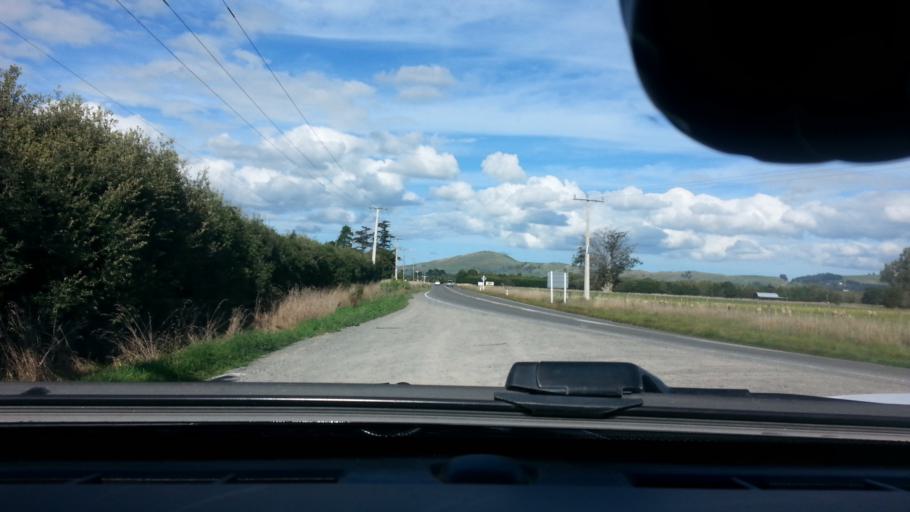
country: NZ
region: Wellington
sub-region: Masterton District
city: Masterton
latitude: -40.9497
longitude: 175.6965
